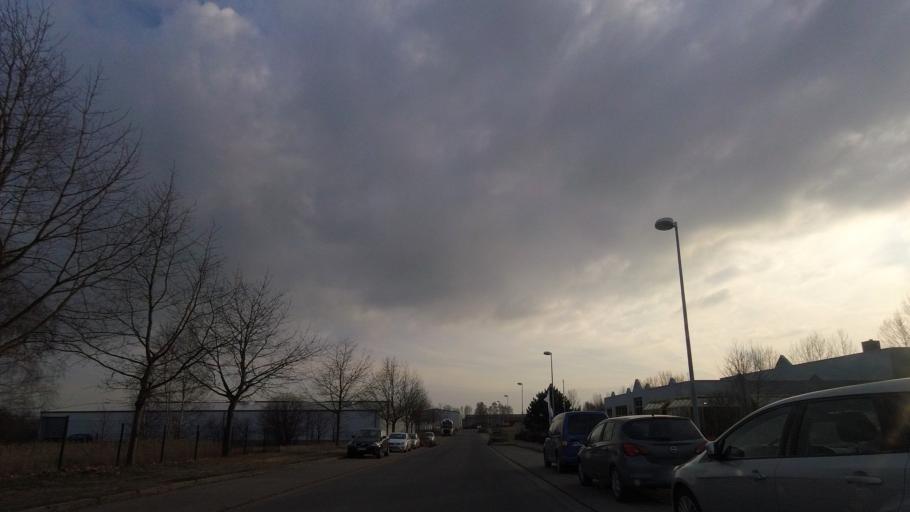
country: DE
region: Brandenburg
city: Wiesenburg
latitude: 52.1172
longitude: 12.4661
